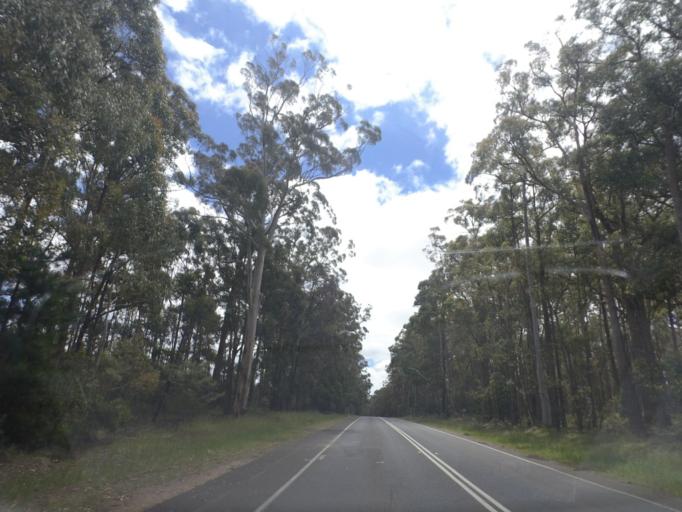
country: AU
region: Victoria
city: Brown Hill
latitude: -37.4971
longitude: 144.1552
